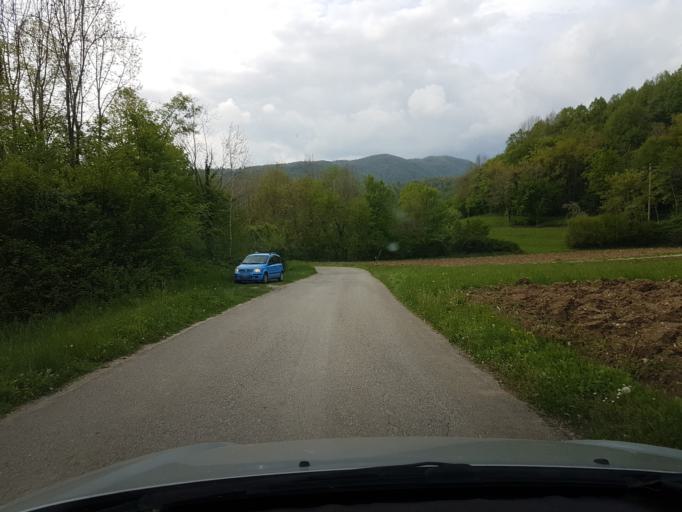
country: IT
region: Friuli Venezia Giulia
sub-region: Provincia di Udine
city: San Leonardo
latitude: 46.1157
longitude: 13.5330
